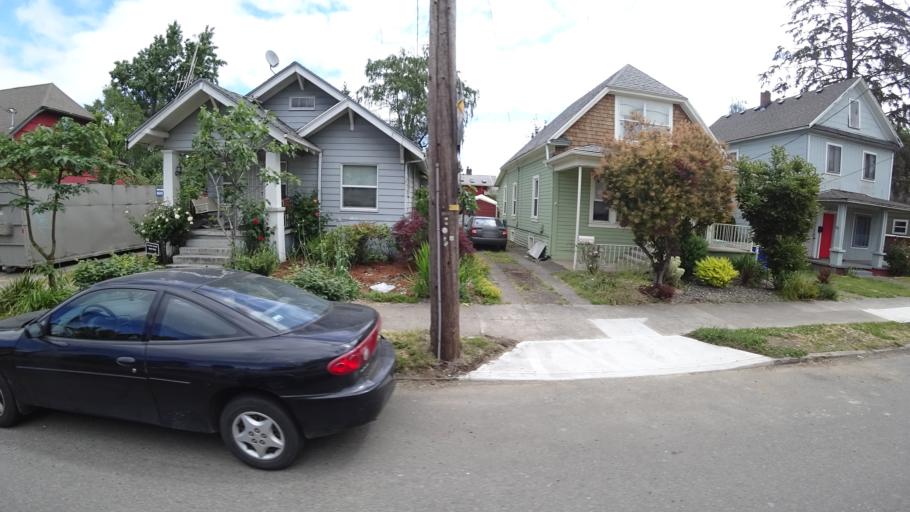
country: US
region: Oregon
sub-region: Washington County
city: West Haven
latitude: 45.5957
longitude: -122.7603
